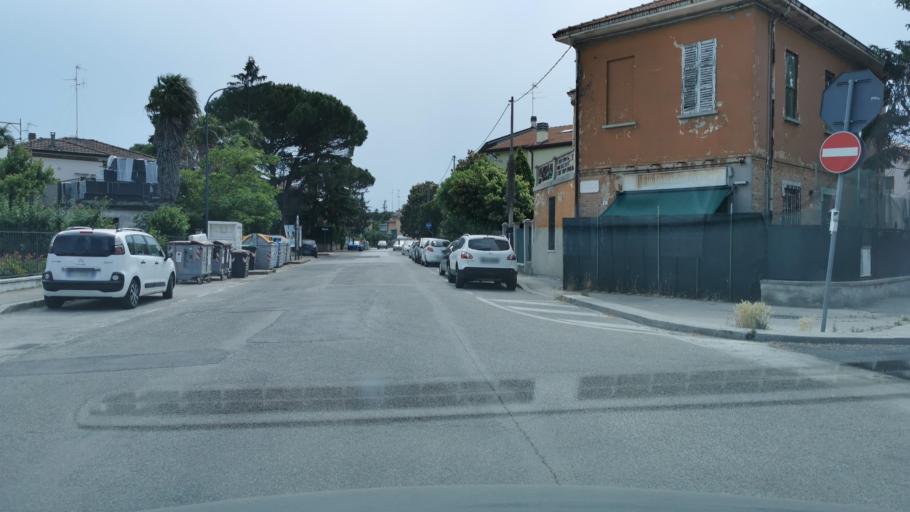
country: IT
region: Emilia-Romagna
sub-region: Provincia di Ravenna
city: Ravenna
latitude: 44.4096
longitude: 12.1981
